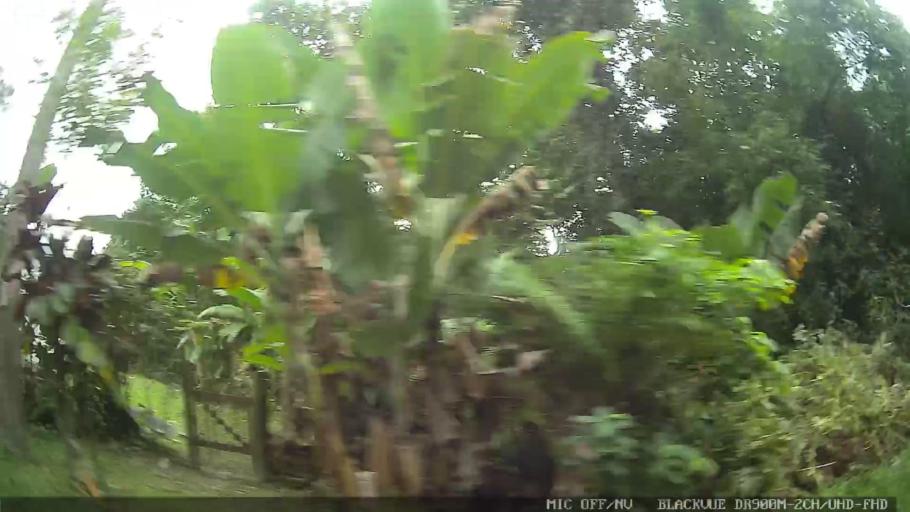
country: BR
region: Sao Paulo
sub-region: Iguape
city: Iguape
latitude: -24.6867
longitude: -47.5101
